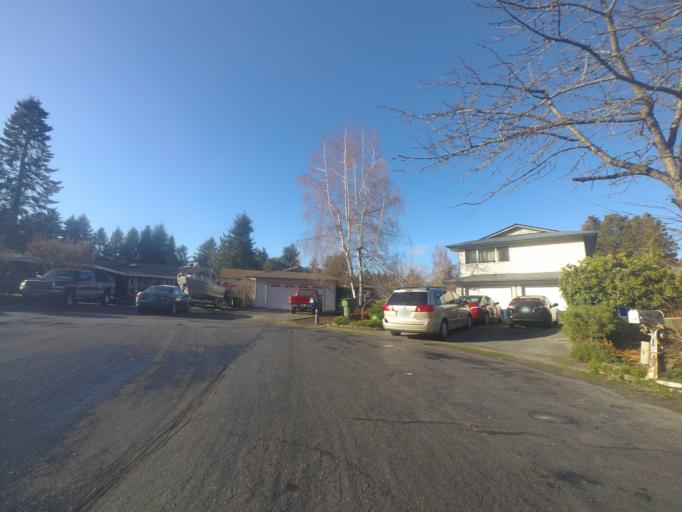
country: US
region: Washington
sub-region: Pierce County
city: University Place
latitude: 47.2258
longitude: -122.5407
